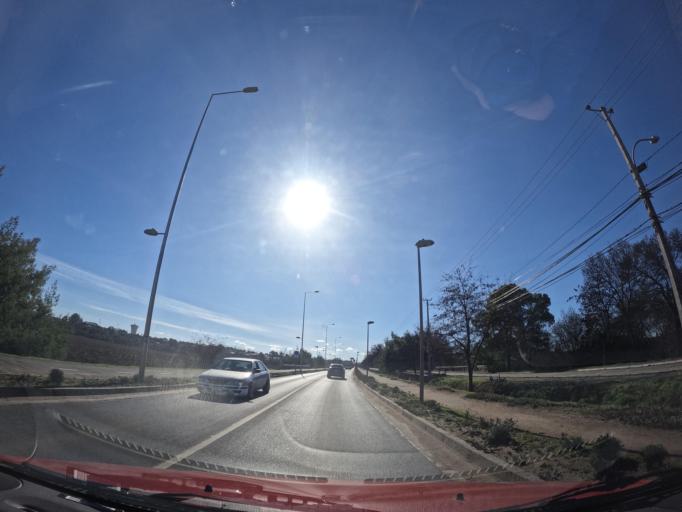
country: CL
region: Maule
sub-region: Provincia de Cauquenes
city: Cauquenes
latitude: -35.9782
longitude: -72.3155
